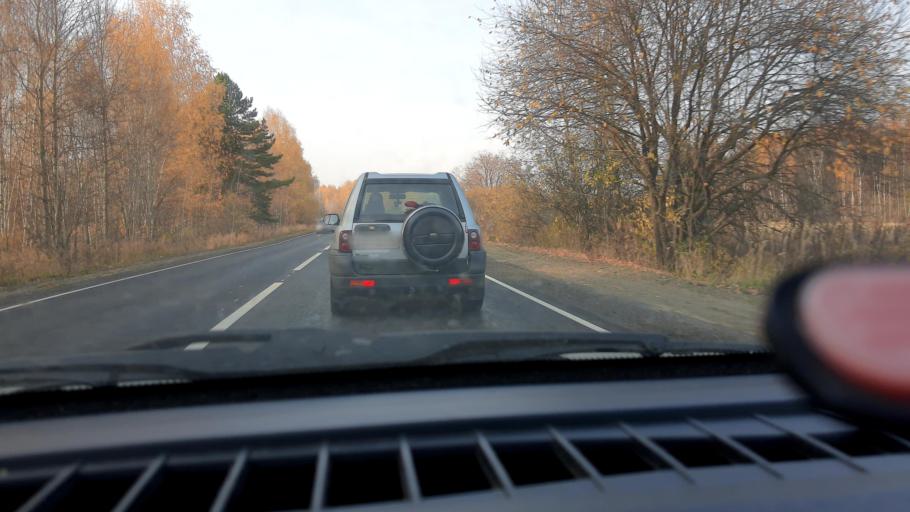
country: RU
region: Nizjnij Novgorod
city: Lukino
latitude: 56.5473
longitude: 43.7563
